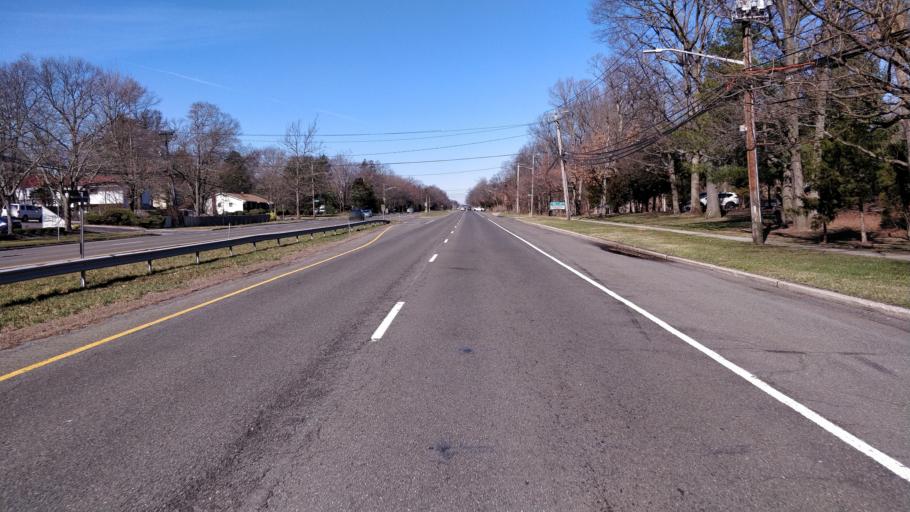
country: US
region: New York
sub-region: Suffolk County
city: Commack
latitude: 40.8331
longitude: -73.2608
